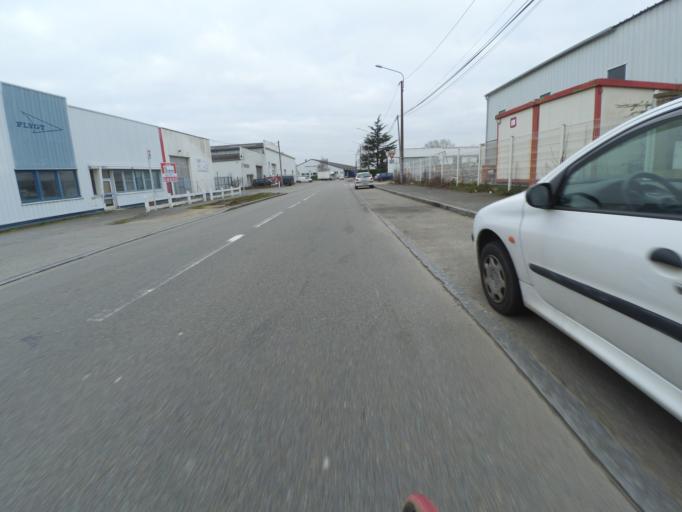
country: FR
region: Pays de la Loire
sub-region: Departement de la Loire-Atlantique
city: Sainte-Luce-sur-Loire
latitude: 47.2663
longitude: -1.4933
